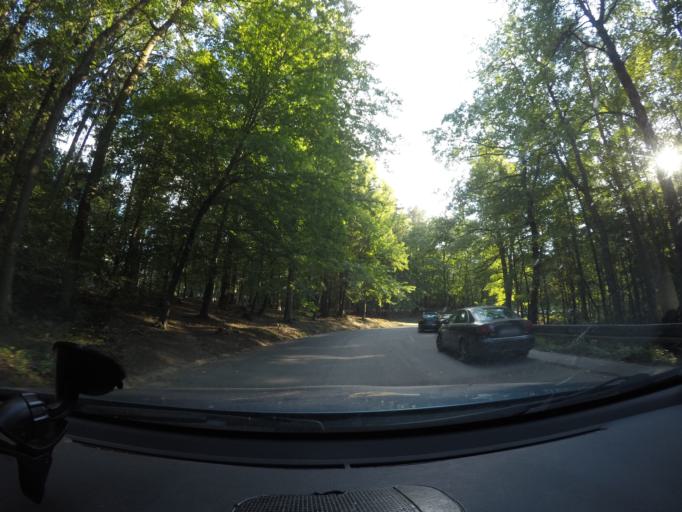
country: SK
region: Trenciansky
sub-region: Okres Trencin
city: Trencin
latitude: 48.8837
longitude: 18.0497
